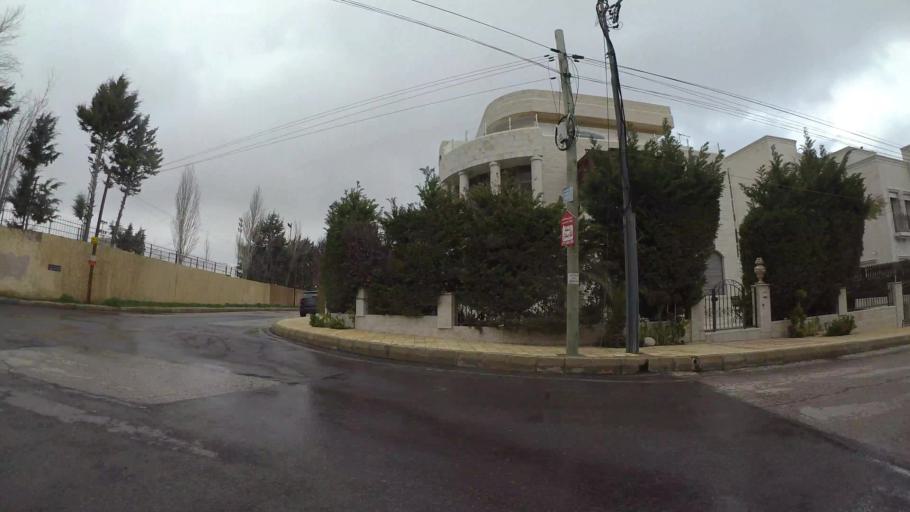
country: JO
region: Amman
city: Amman
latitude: 31.9465
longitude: 35.8974
